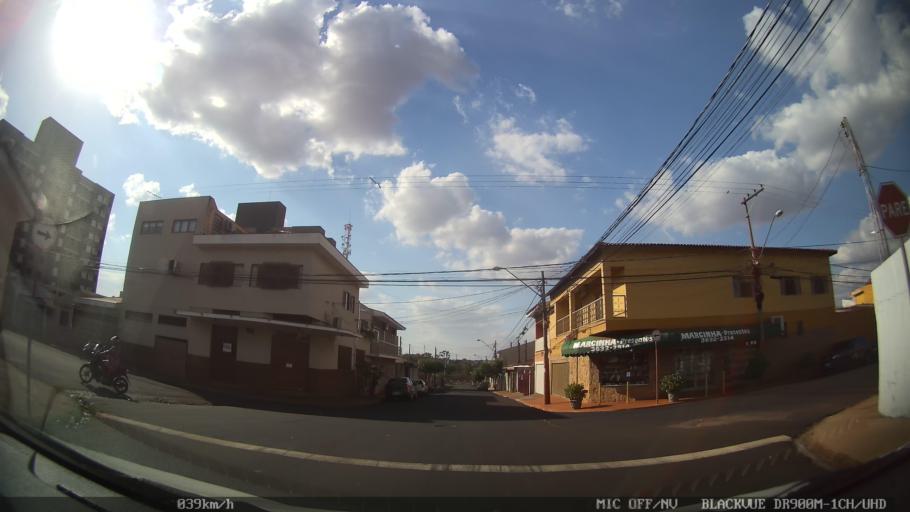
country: BR
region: Sao Paulo
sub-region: Ribeirao Preto
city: Ribeirao Preto
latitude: -21.1813
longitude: -47.8276
